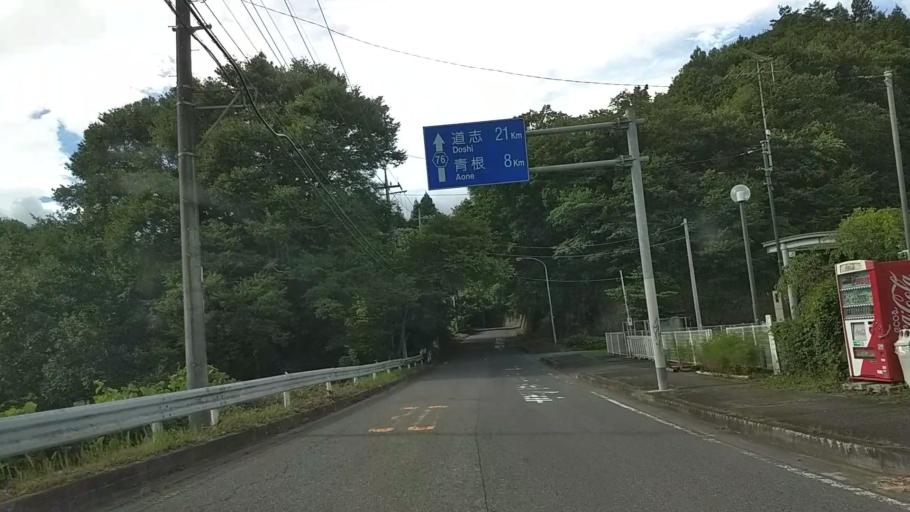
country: JP
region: Yamanashi
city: Uenohara
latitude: 35.5803
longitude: 139.1506
